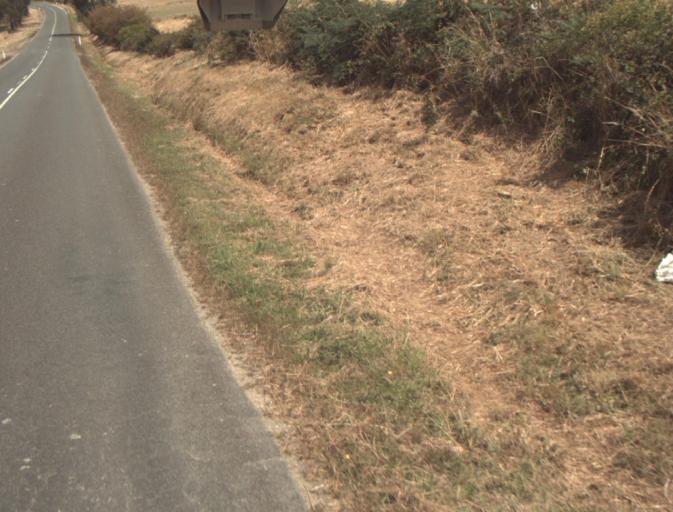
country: AU
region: Tasmania
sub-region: Launceston
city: Mayfield
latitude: -41.2206
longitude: 147.1215
